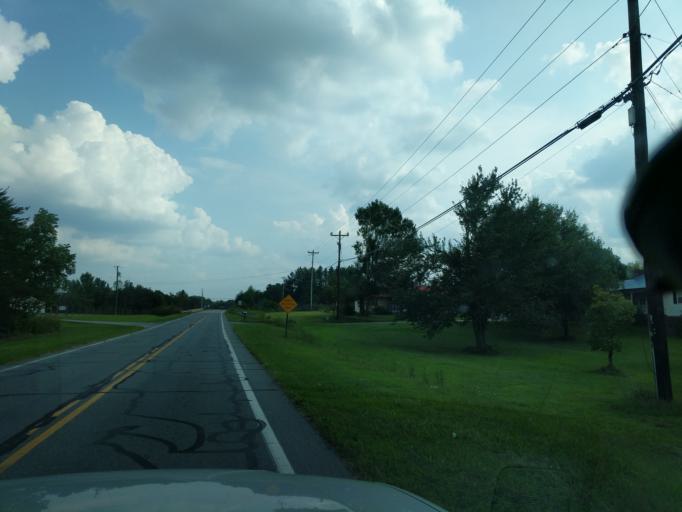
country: US
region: North Carolina
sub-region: Rutherford County
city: Spindale
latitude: 35.3107
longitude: -81.9387
